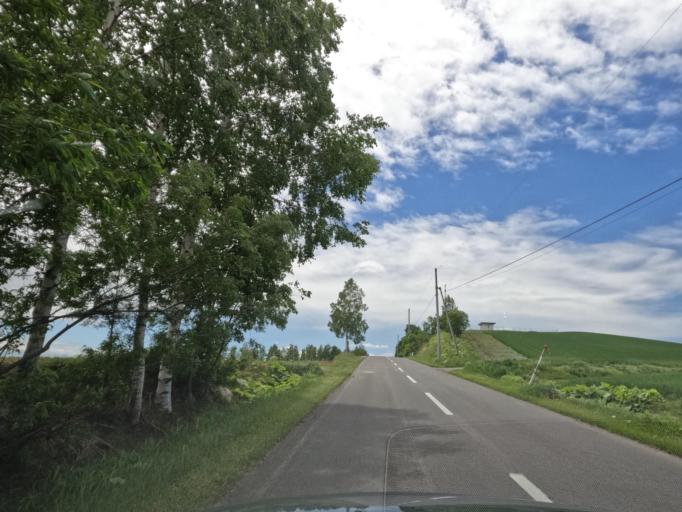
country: JP
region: Hokkaido
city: Shimo-furano
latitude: 43.5214
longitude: 142.4313
